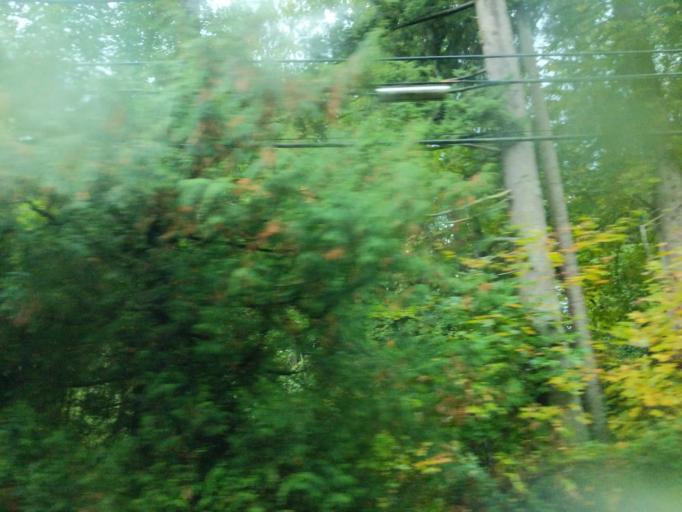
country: US
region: Washington
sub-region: King County
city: Bothell
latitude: 47.7865
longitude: -122.2075
